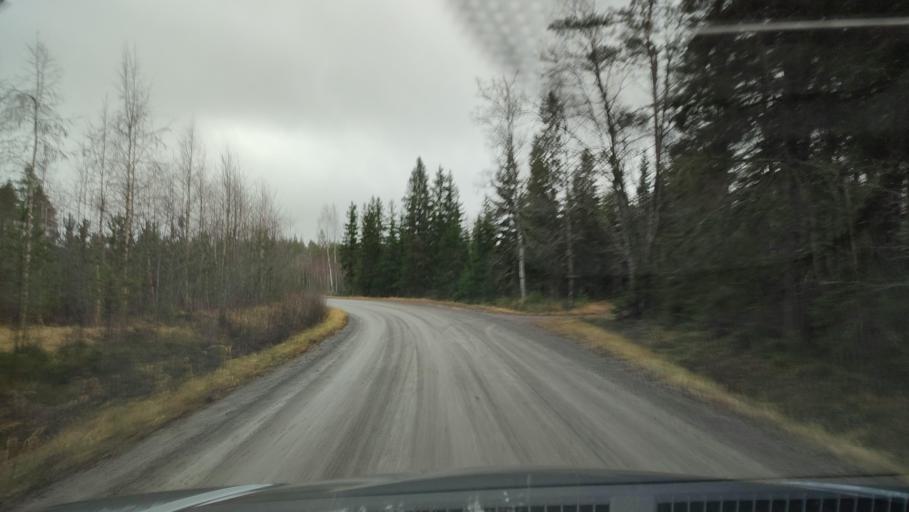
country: FI
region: Southern Ostrobothnia
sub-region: Suupohja
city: Karijoki
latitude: 62.1242
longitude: 21.6006
